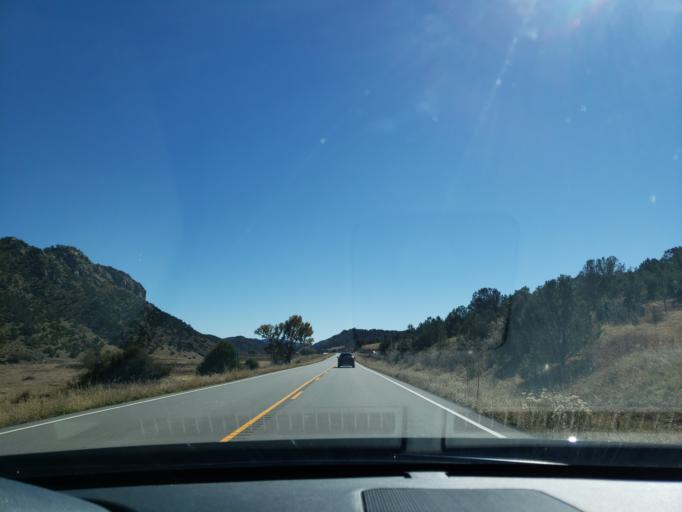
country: US
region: Colorado
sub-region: Fremont County
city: Canon City
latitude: 38.6142
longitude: -105.4437
